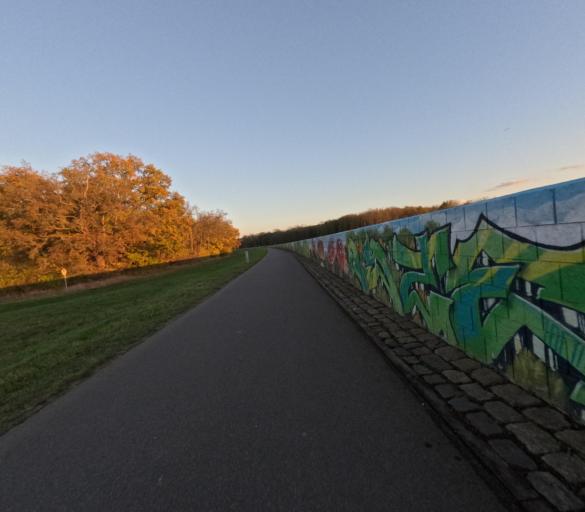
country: DE
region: Saxony
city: Schkeuditz
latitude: 51.3728
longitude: 12.2839
